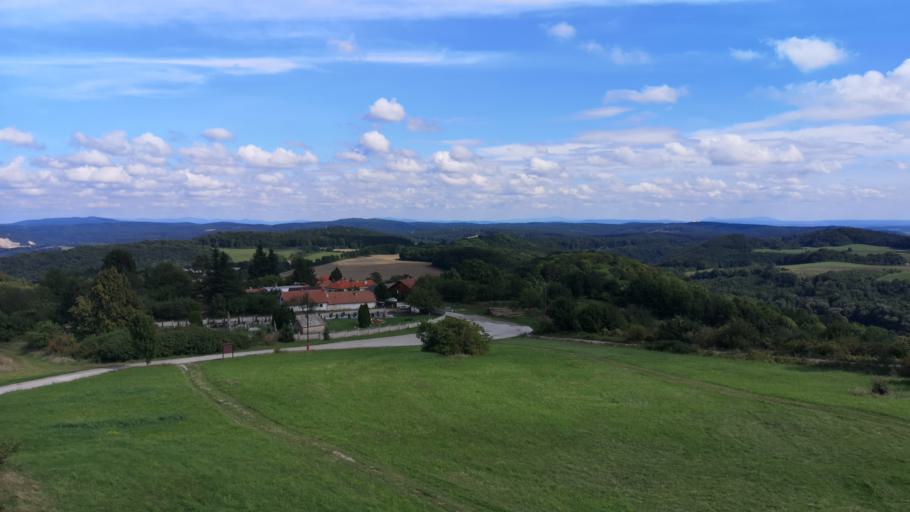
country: SK
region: Trnavsky
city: Smolenice
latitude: 48.5723
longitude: 17.3909
